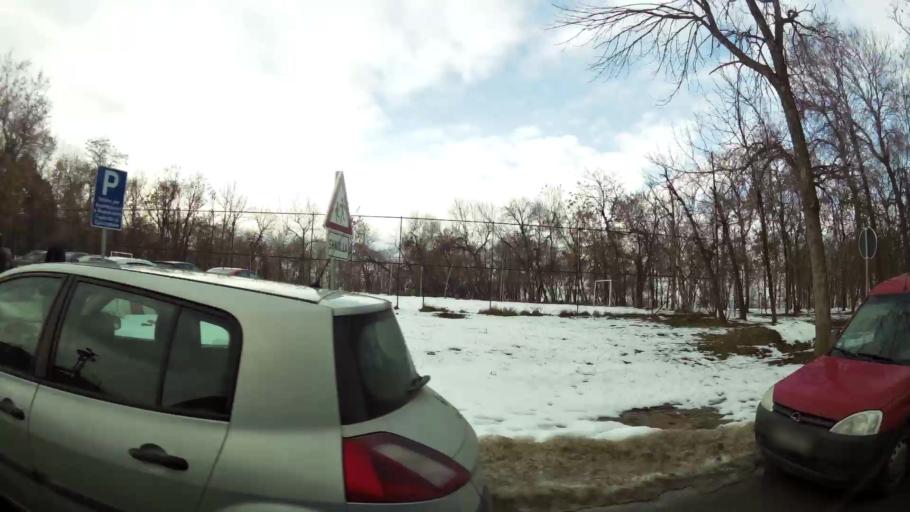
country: XK
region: Pristina
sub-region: Komuna e Prishtines
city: Pristina
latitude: 42.6693
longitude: 21.1529
